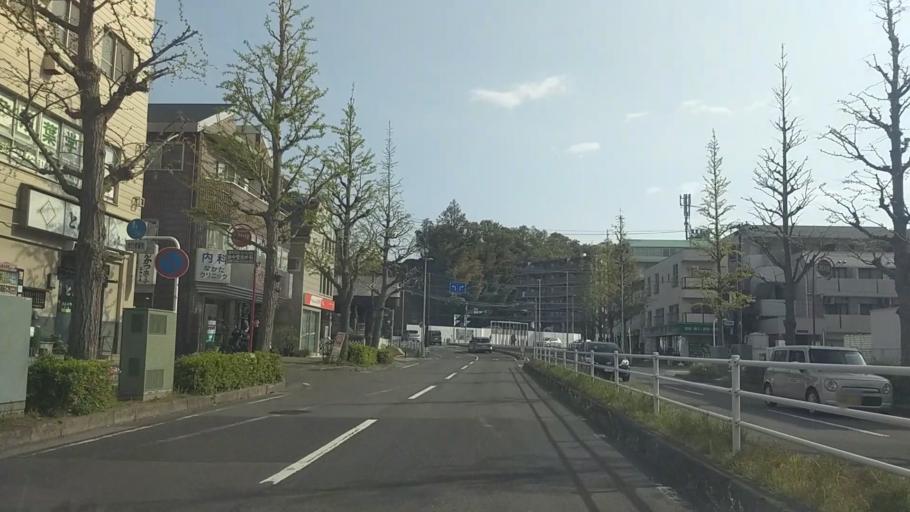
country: JP
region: Kanagawa
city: Kamakura
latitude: 35.3628
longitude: 139.5518
